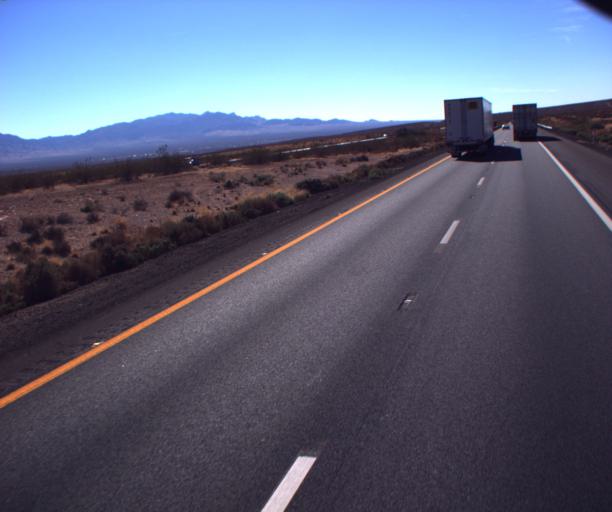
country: US
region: Arizona
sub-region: Mohave County
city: Beaver Dam
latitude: 36.8678
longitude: -113.9677
